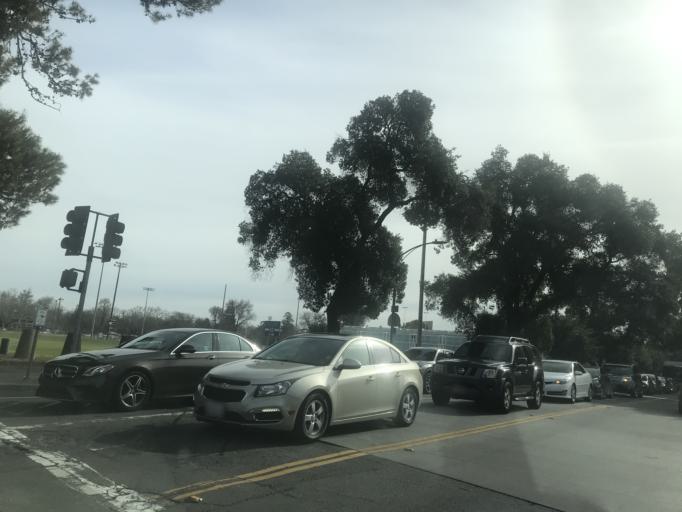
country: US
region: California
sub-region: Yolo County
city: Davis
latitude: 38.5461
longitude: -121.7509
